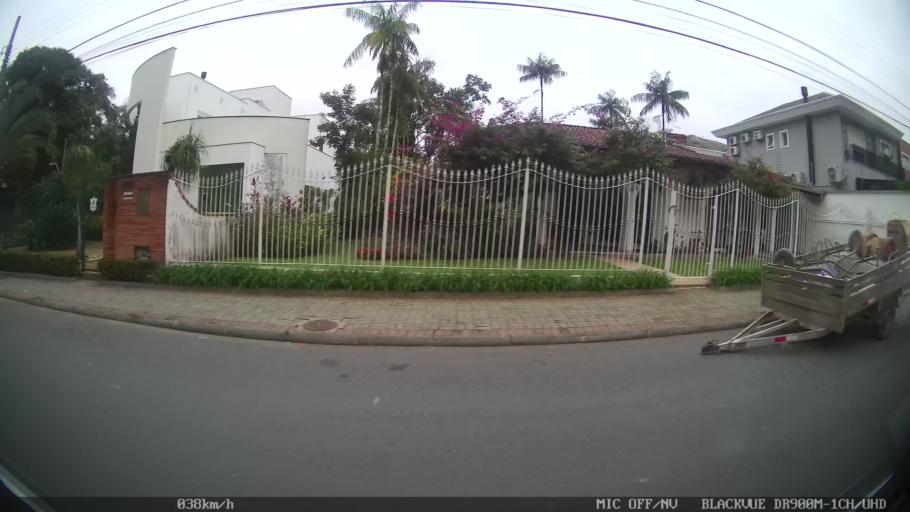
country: BR
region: Santa Catarina
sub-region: Joinville
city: Joinville
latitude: -26.3003
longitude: -48.8614
